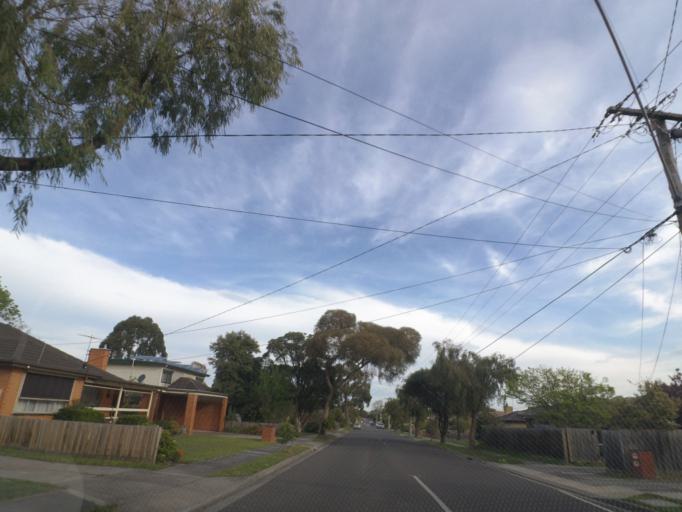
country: AU
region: Victoria
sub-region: Knox
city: Knoxfield
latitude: -37.8922
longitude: 145.2405
